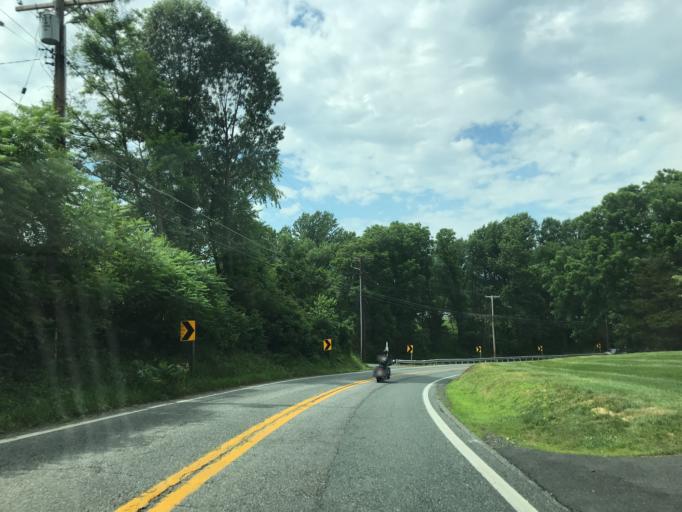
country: US
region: Maryland
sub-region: Harford County
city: Bel Air North
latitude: 39.6040
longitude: -76.3974
